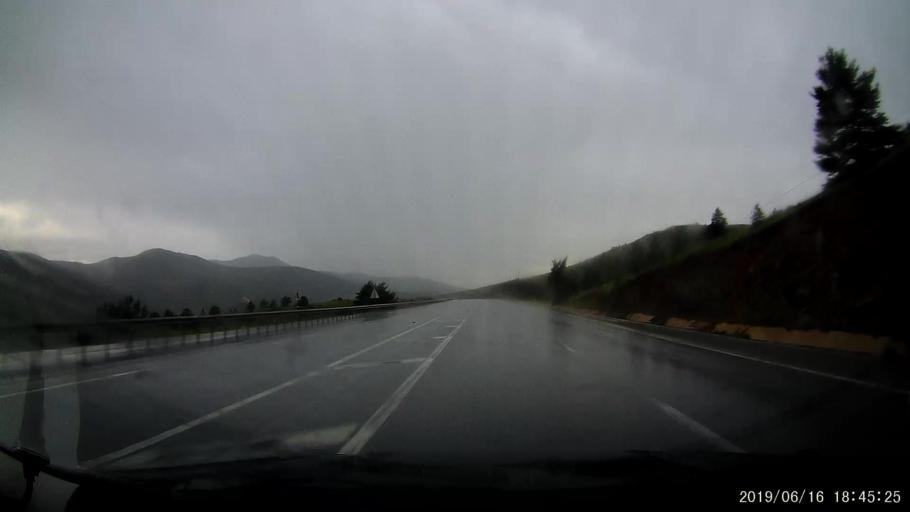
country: TR
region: Erzincan
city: Doganbeyli
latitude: 39.8705
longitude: 39.0570
